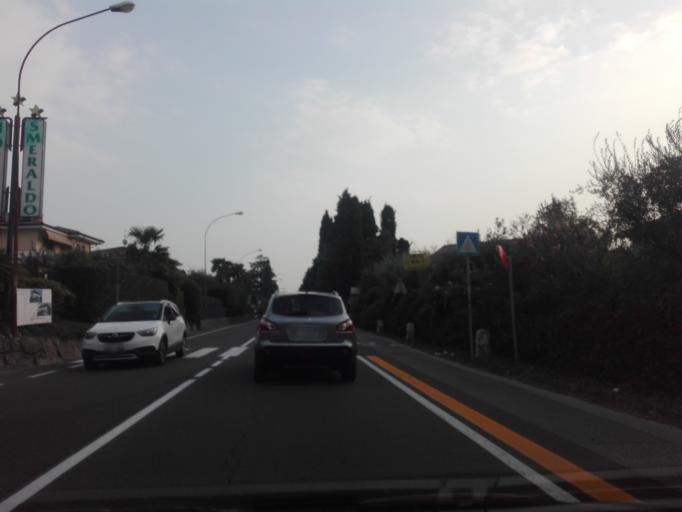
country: IT
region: Veneto
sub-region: Provincia di Verona
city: Lazise
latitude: 45.5103
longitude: 10.7334
